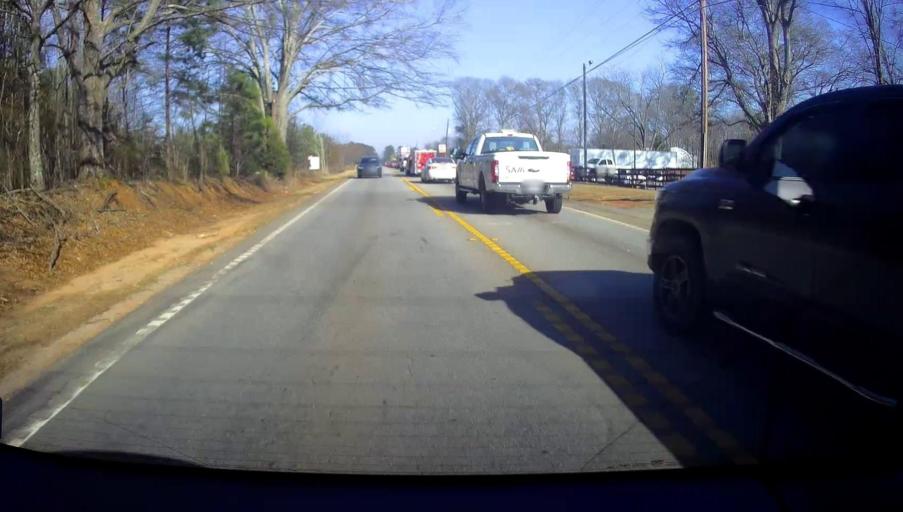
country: US
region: Georgia
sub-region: Henry County
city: Locust Grove
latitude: 33.3208
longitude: -84.0477
